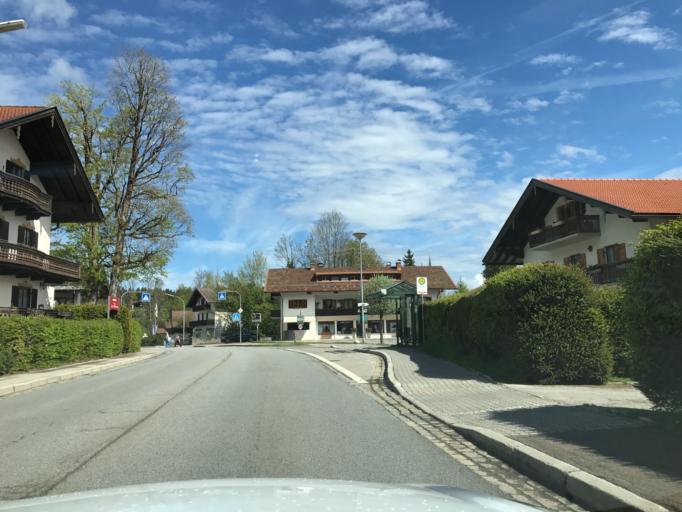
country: DE
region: Bavaria
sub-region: Upper Bavaria
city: Bad Wiessee
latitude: 47.7015
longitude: 11.7277
